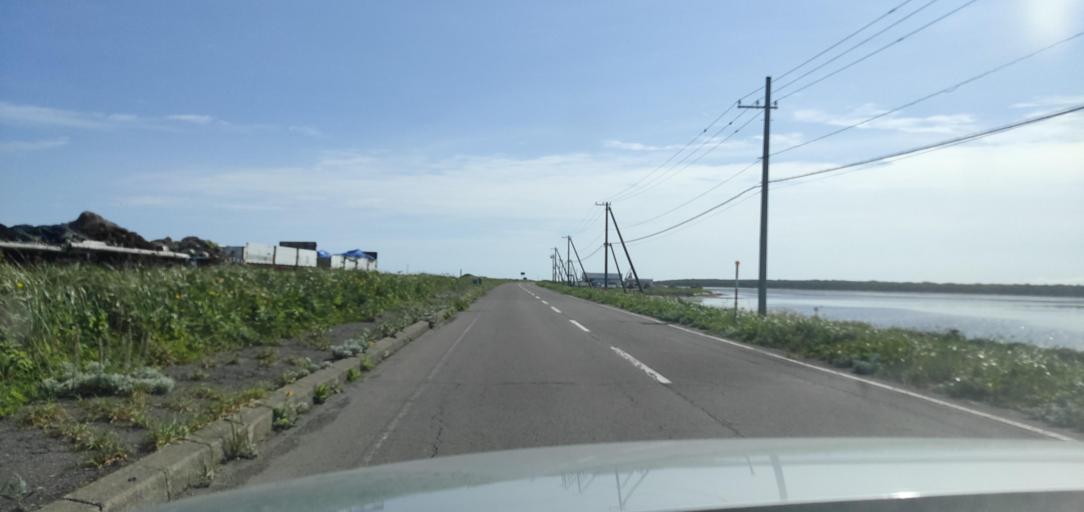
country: JP
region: Hokkaido
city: Shibetsu
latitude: 43.6134
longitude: 145.2523
